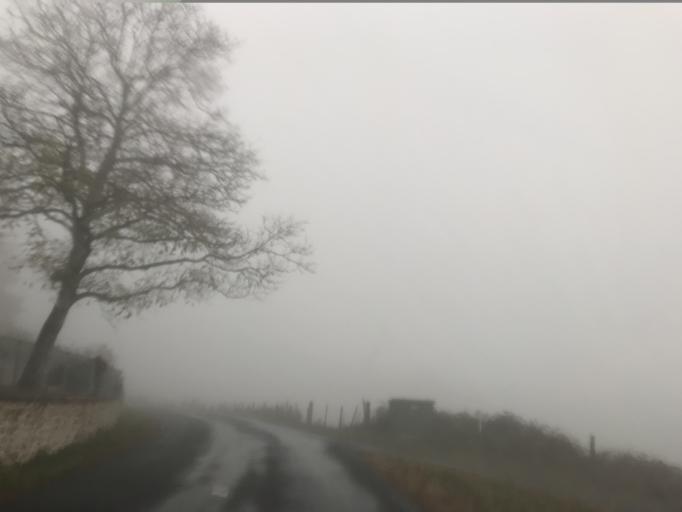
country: FR
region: Auvergne
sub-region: Departement du Puy-de-Dome
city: Escoutoux
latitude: 45.7850
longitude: 3.6202
